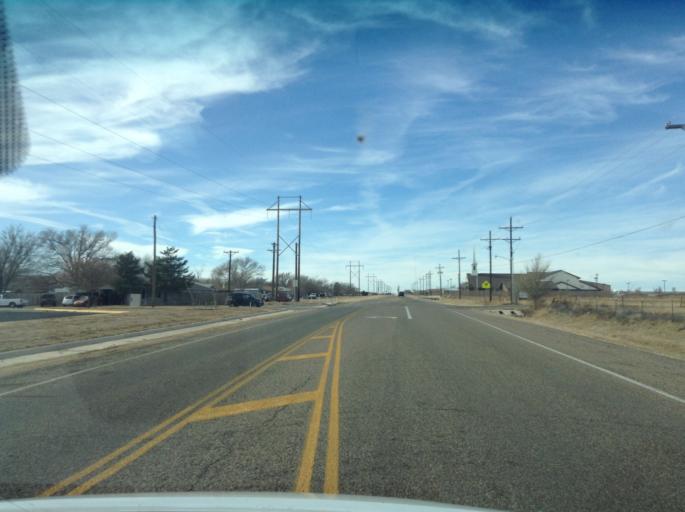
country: US
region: Texas
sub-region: Randall County
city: Canyon
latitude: 34.9995
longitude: -101.9296
